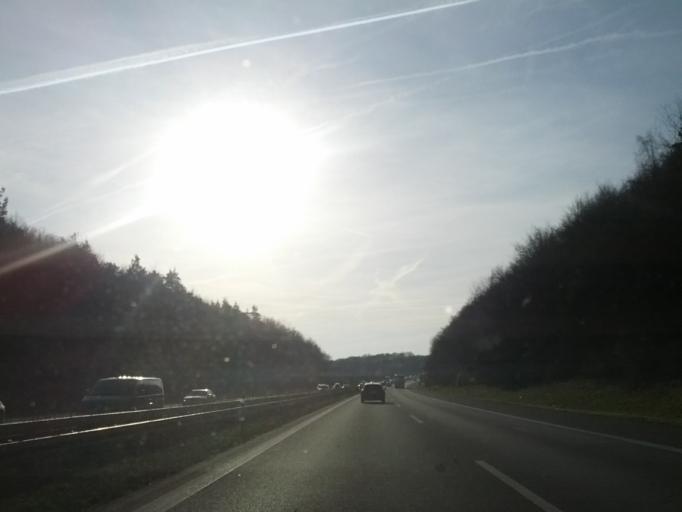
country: DE
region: Bavaria
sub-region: Regierungsbezirk Unterfranken
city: Unterpleichfeld
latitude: 49.8934
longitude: 10.0010
